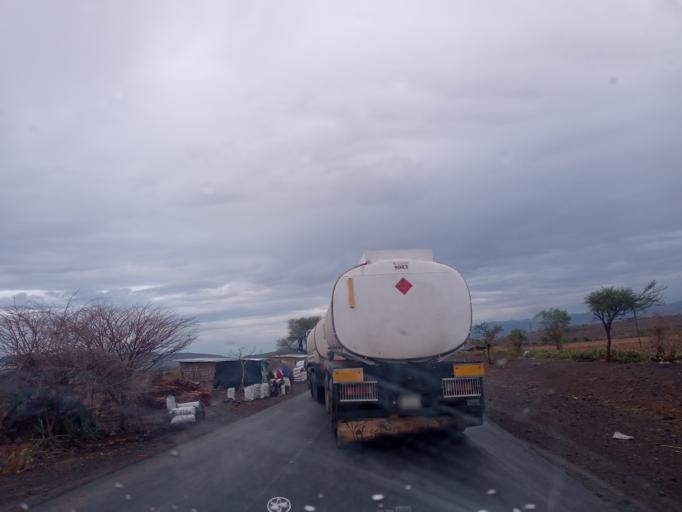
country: ET
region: Oromiya
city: Asbe Teferi
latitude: 9.2019
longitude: 40.6844
